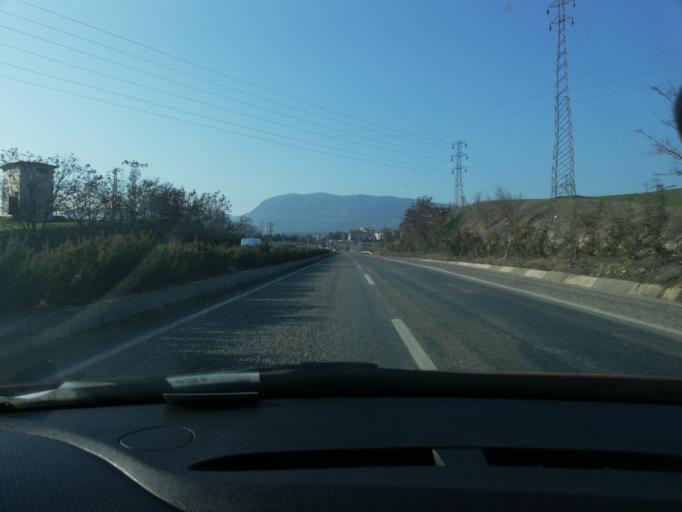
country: TR
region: Karabuk
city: Safranbolu
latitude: 41.2371
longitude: 32.7044
